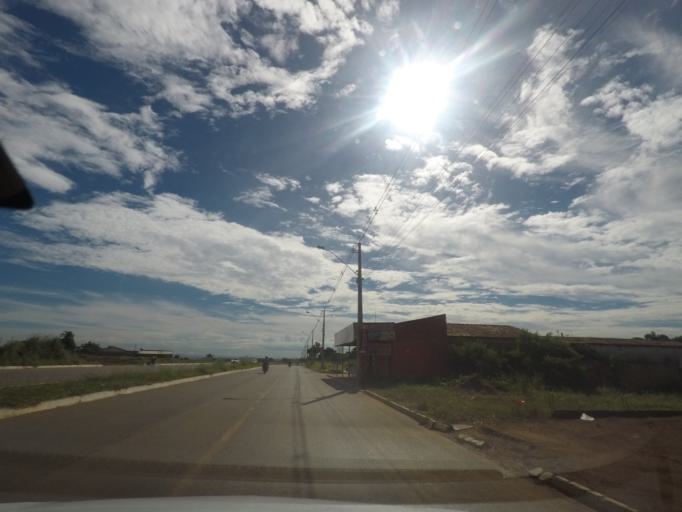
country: BR
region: Goias
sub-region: Aparecida De Goiania
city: Aparecida de Goiania
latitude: -16.8105
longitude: -49.2794
